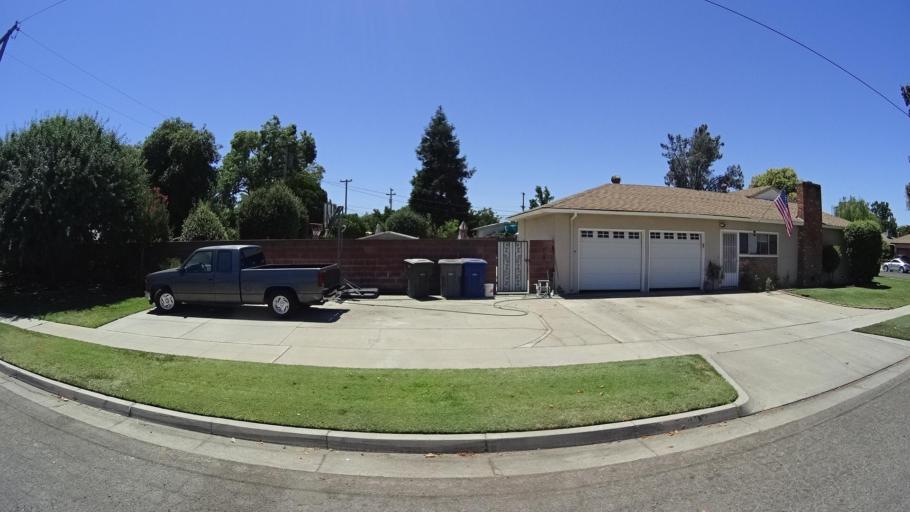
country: US
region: California
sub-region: Fresno County
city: Fresno
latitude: 36.8056
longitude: -119.7640
